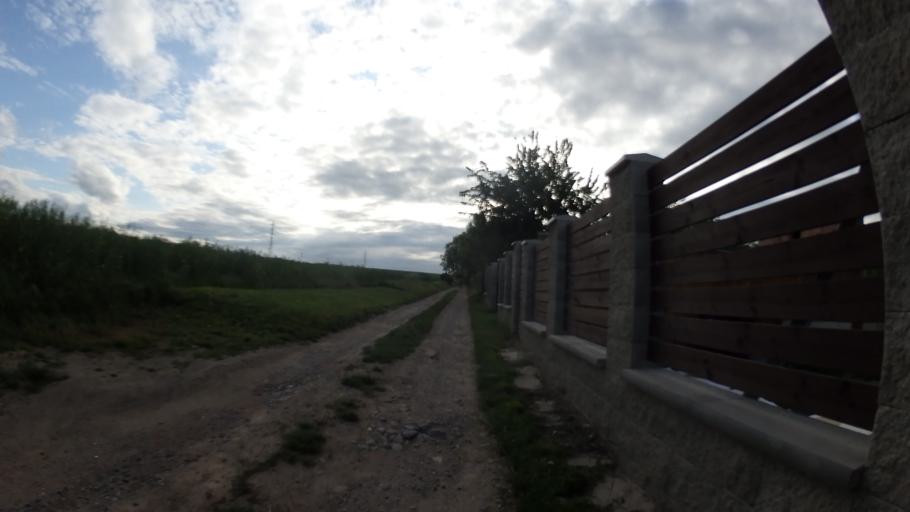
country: CZ
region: South Moravian
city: Moravany
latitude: 49.1589
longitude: 16.5930
